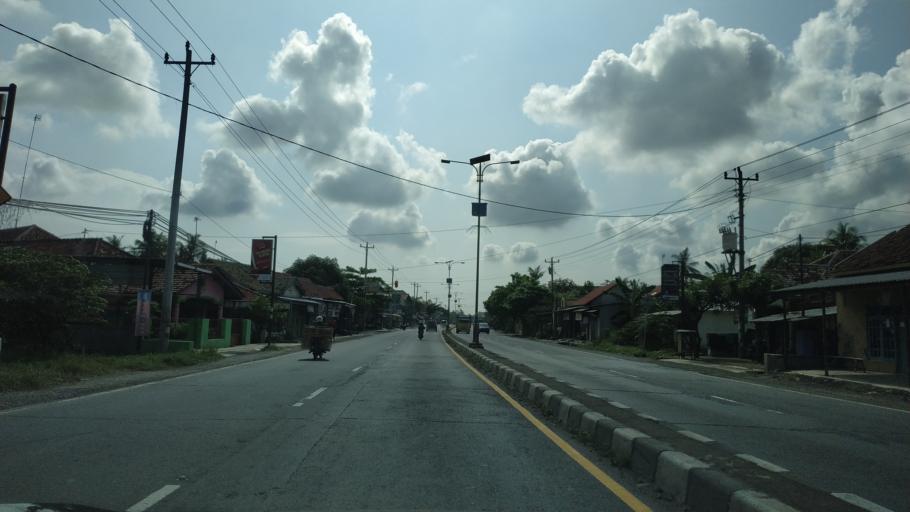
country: ID
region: Central Java
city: Comal
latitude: -6.8890
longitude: 109.5450
